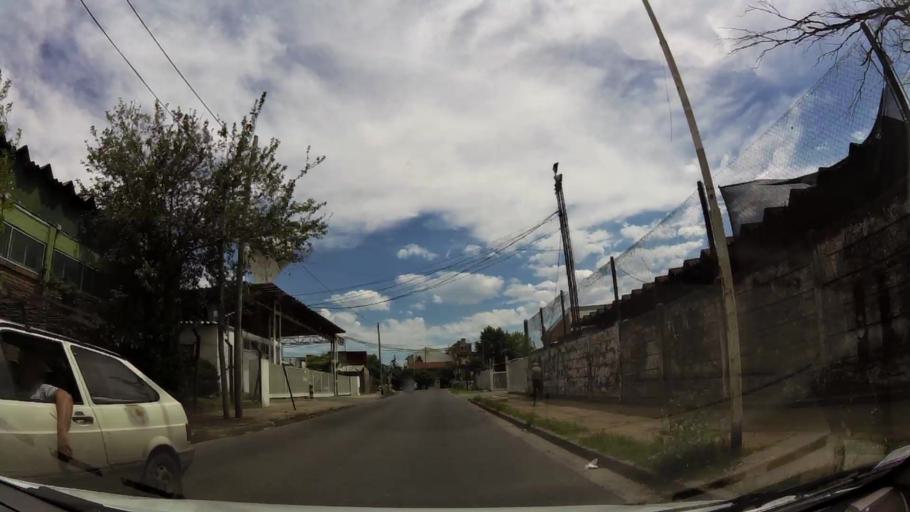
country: AR
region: Buenos Aires
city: San Justo
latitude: -34.6817
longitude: -58.5420
